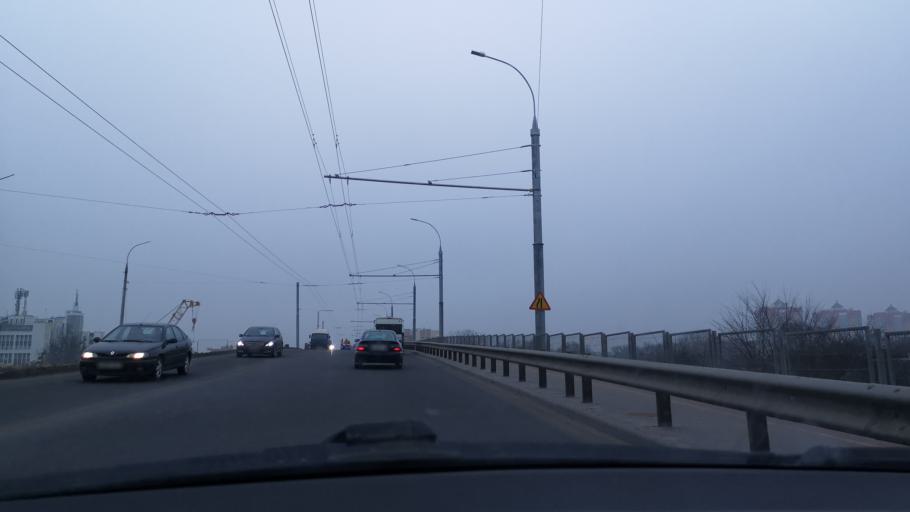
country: BY
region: Brest
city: Brest
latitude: 52.0908
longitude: 23.7174
